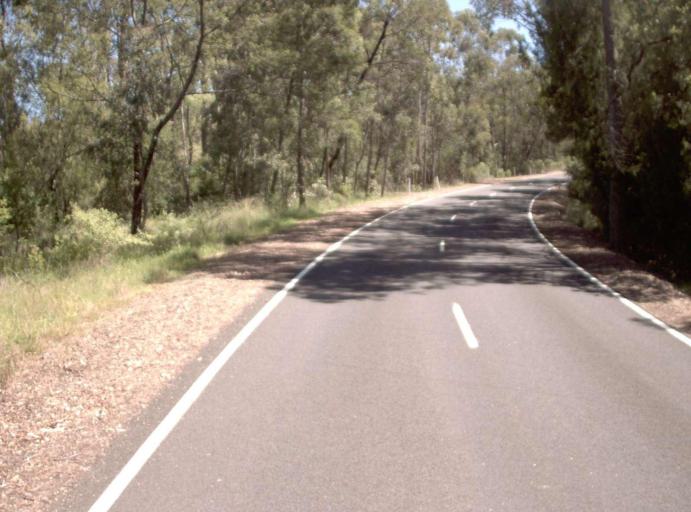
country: AU
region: Victoria
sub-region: East Gippsland
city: Lakes Entrance
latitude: -37.3536
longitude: 148.2281
